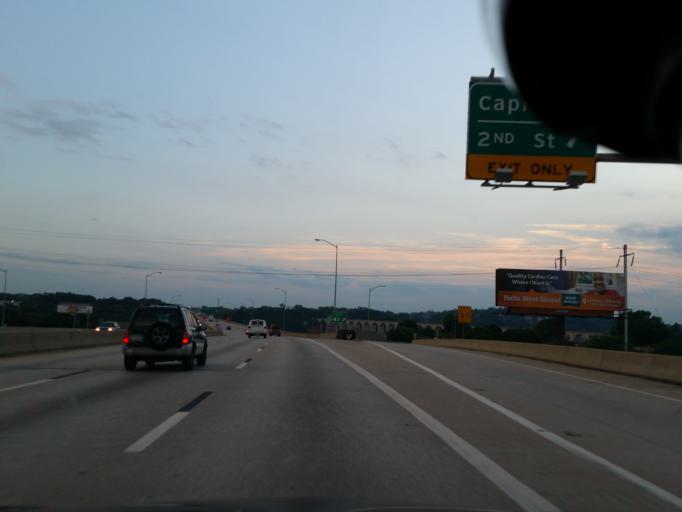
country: US
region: Pennsylvania
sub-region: Cumberland County
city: New Cumberland
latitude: 40.2526
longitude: -76.8698
